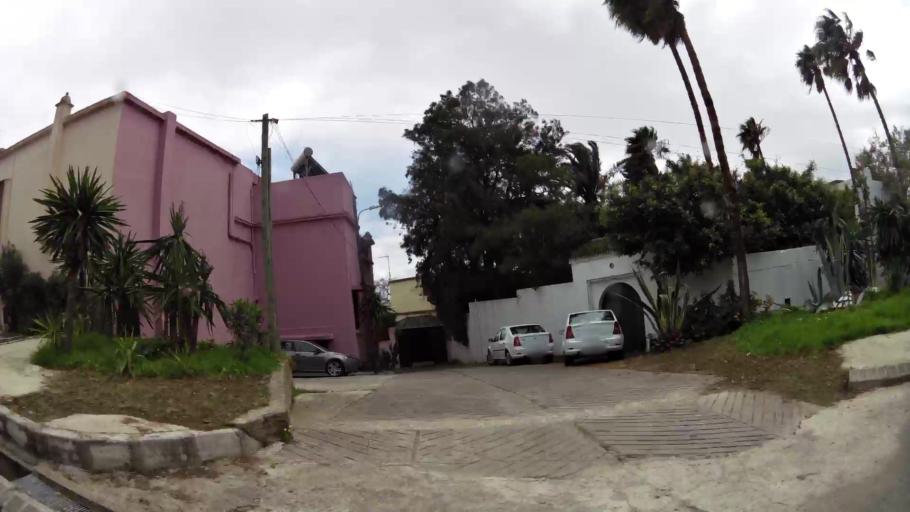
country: MA
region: Tanger-Tetouan
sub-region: Tanger-Assilah
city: Tangier
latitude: 35.7848
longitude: -5.8488
